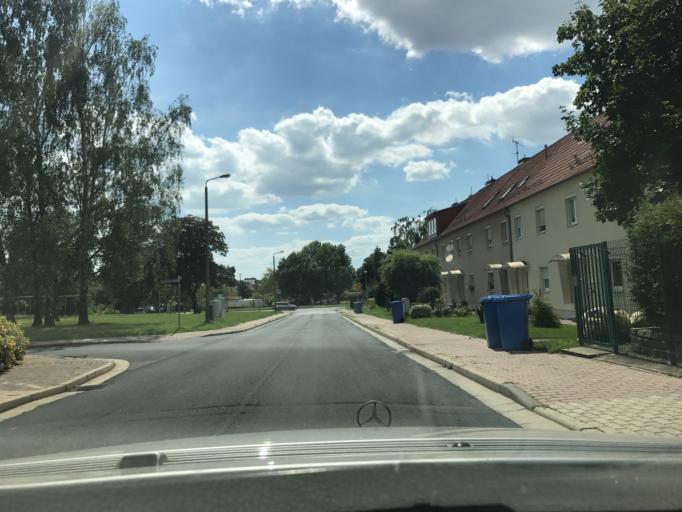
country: DE
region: Thuringia
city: Muehlhausen
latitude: 51.2164
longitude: 10.4726
